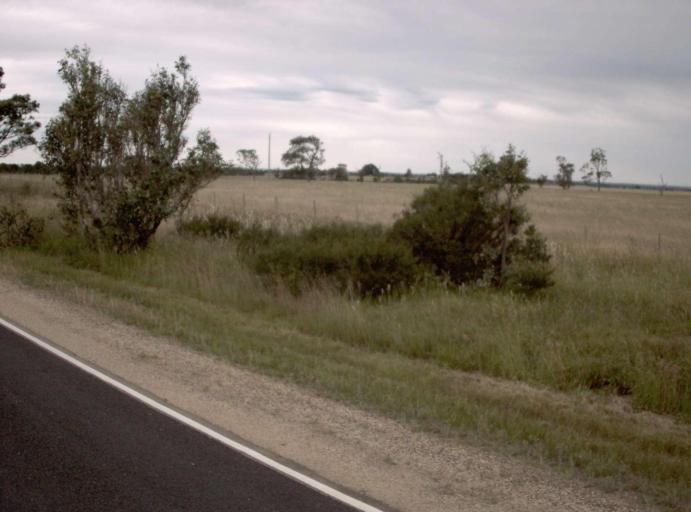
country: AU
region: Victoria
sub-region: Wellington
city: Sale
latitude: -37.9980
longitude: 147.2129
